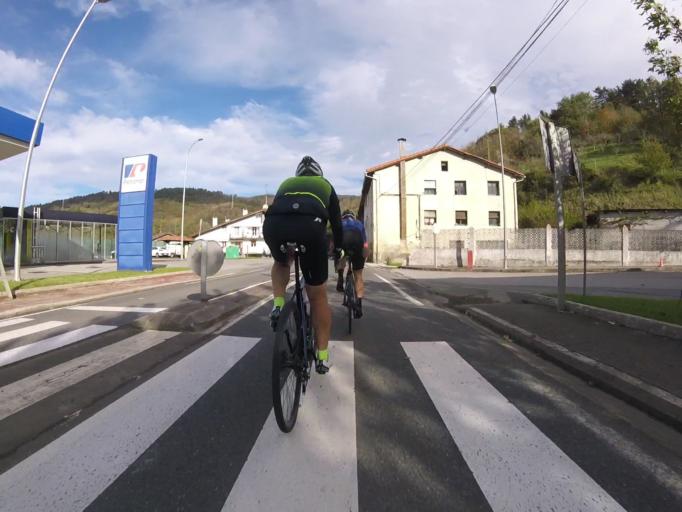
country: ES
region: Basque Country
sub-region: Provincia de Guipuzcoa
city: Usurbil
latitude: 43.2784
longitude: -2.0727
